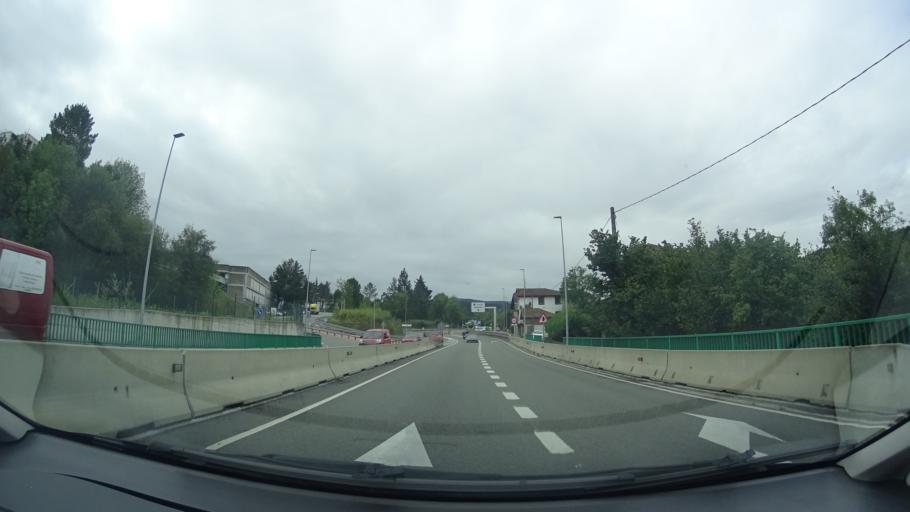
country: ES
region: Basque Country
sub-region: Bizkaia
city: Galdakao
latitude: 43.2250
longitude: -2.8200
